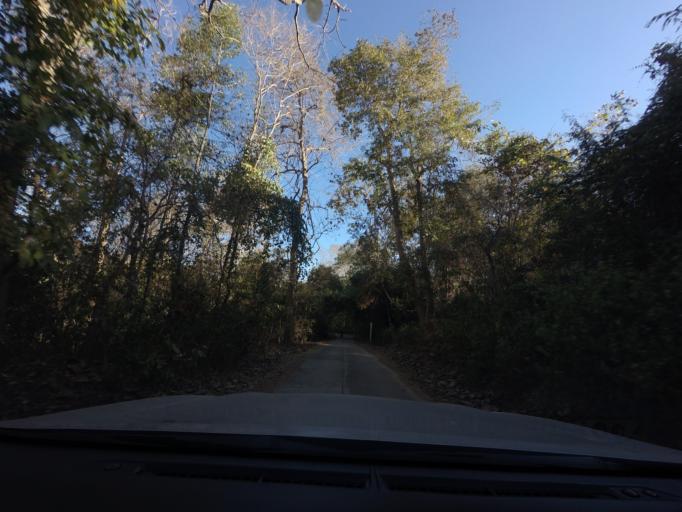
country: TH
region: Mae Hong Son
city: Wiang Nuea
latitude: 19.4001
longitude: 98.4189
